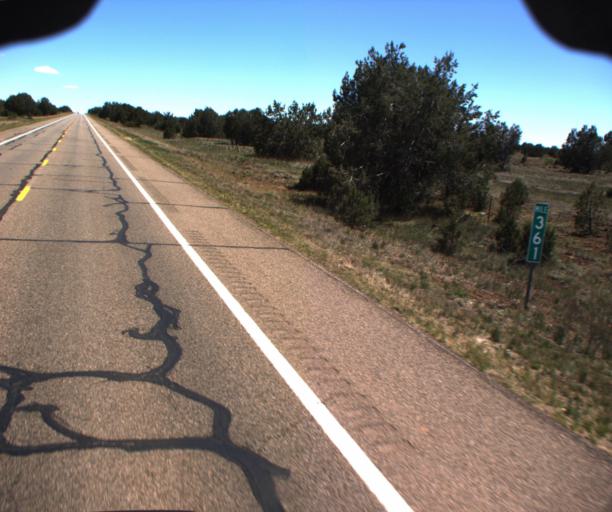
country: US
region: Arizona
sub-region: Coconino County
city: Williams
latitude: 35.1814
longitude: -112.4656
